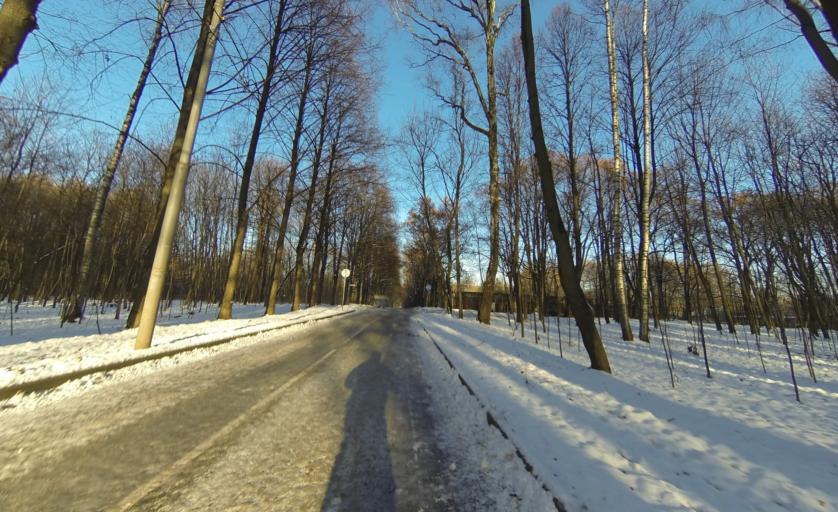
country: RU
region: Moscow
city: Sokol'niki
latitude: 55.8030
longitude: 37.6799
